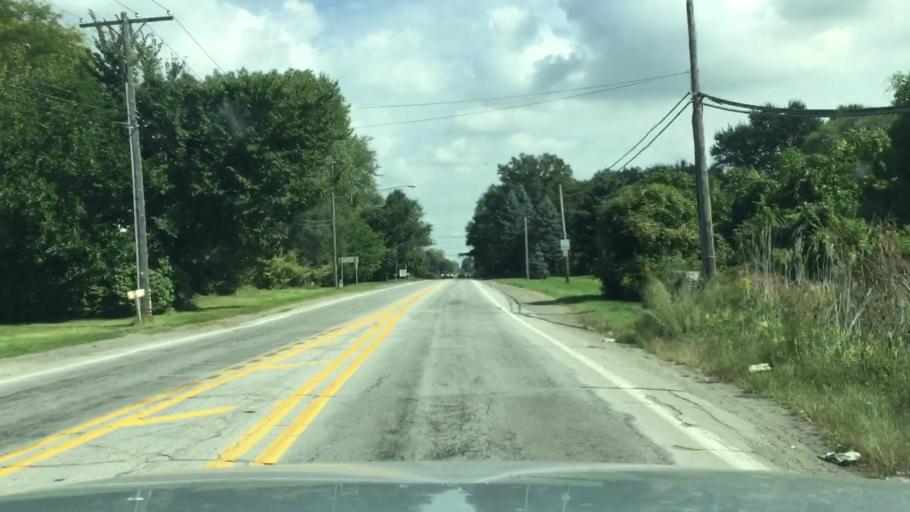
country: US
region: Michigan
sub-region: Wayne County
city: Wayne
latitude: 42.2520
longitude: -83.3863
